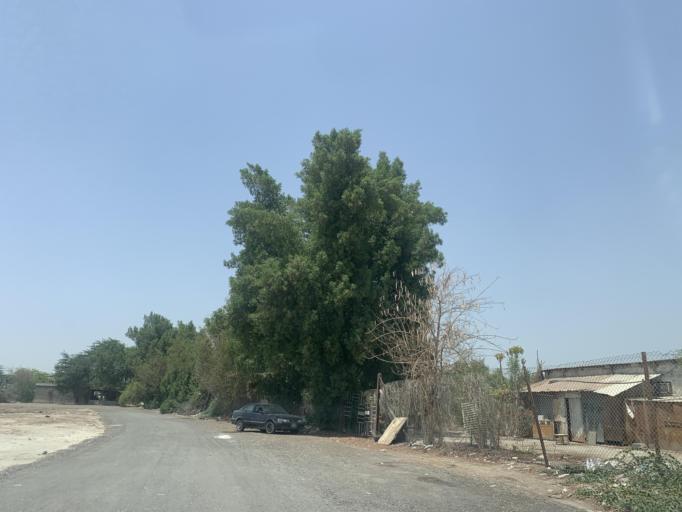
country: BH
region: Central Governorate
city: Madinat Hamad
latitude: 26.1551
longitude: 50.4933
